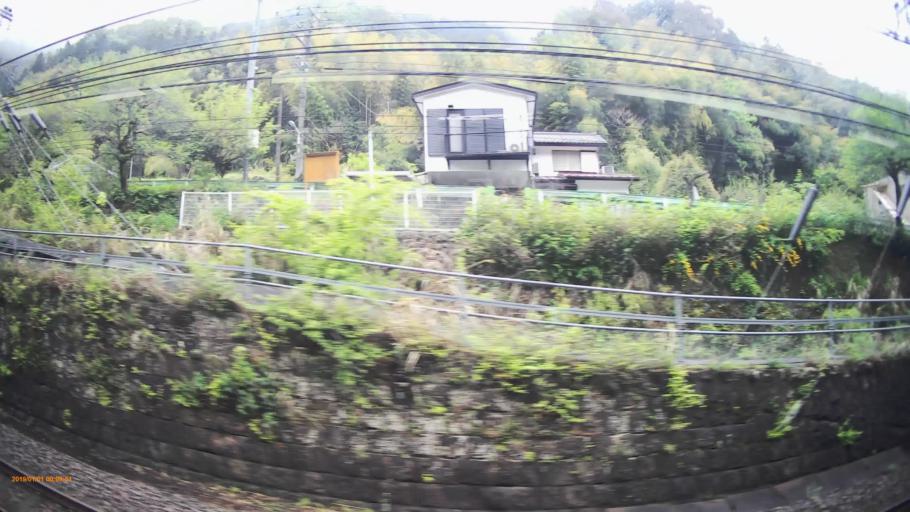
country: JP
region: Tokyo
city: Itsukaichi
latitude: 35.6396
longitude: 139.2343
